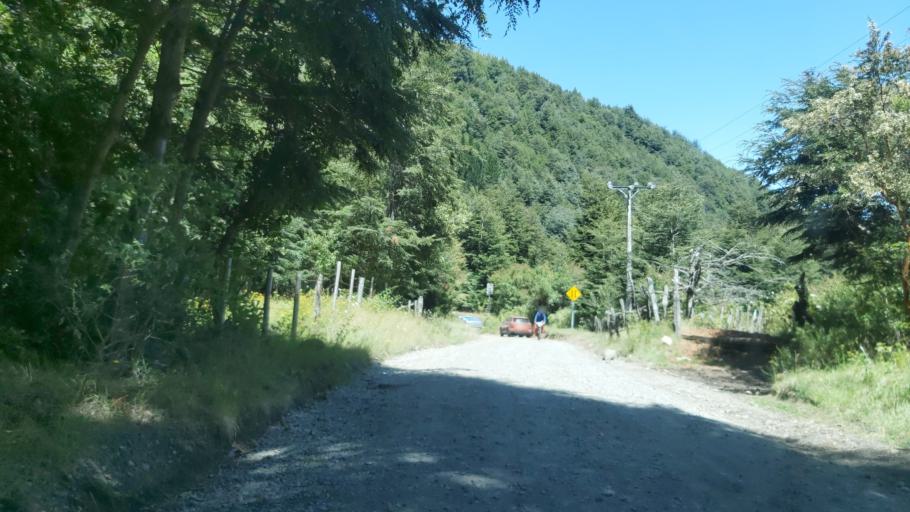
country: CL
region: Araucania
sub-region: Provincia de Cautin
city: Vilcun
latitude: -38.4733
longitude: -71.6734
